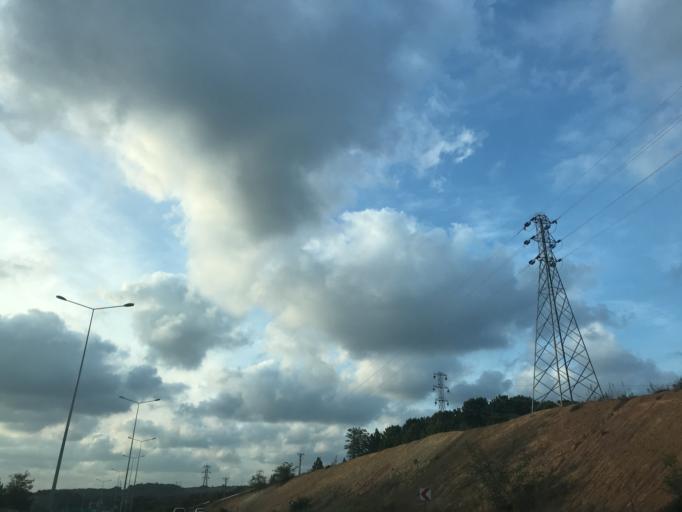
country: TR
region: Istanbul
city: Kemerburgaz
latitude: 41.1976
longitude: 28.8667
